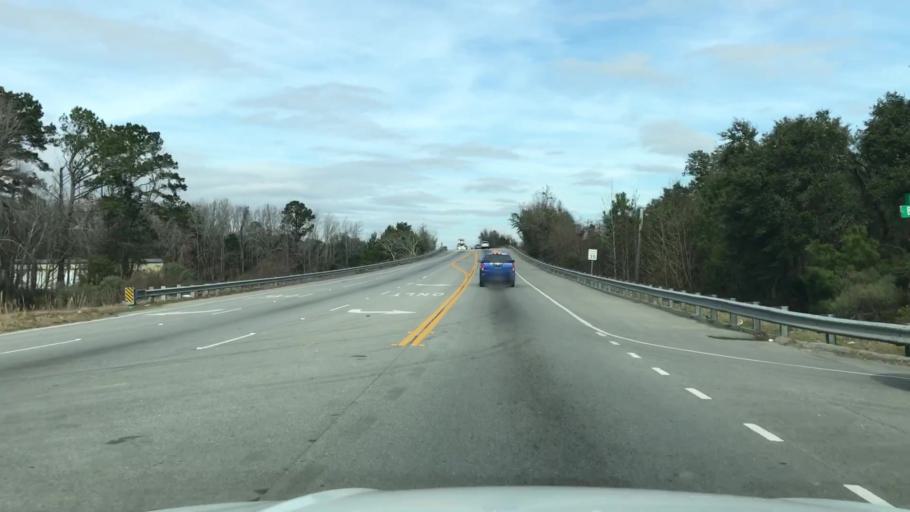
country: US
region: South Carolina
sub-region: Charleston County
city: Shell Point
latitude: 32.7907
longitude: -80.1080
